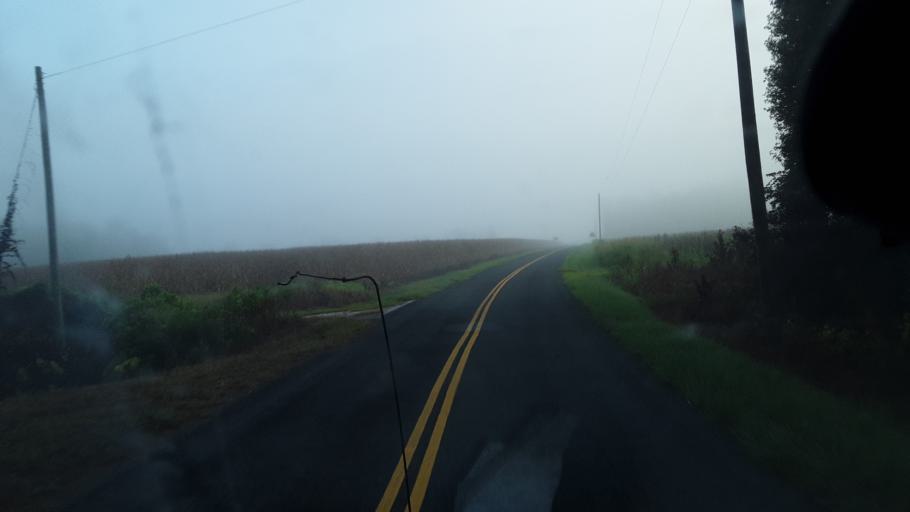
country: US
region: South Carolina
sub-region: Williamsburg County
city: Kingstree
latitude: 33.8049
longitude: -79.9643
